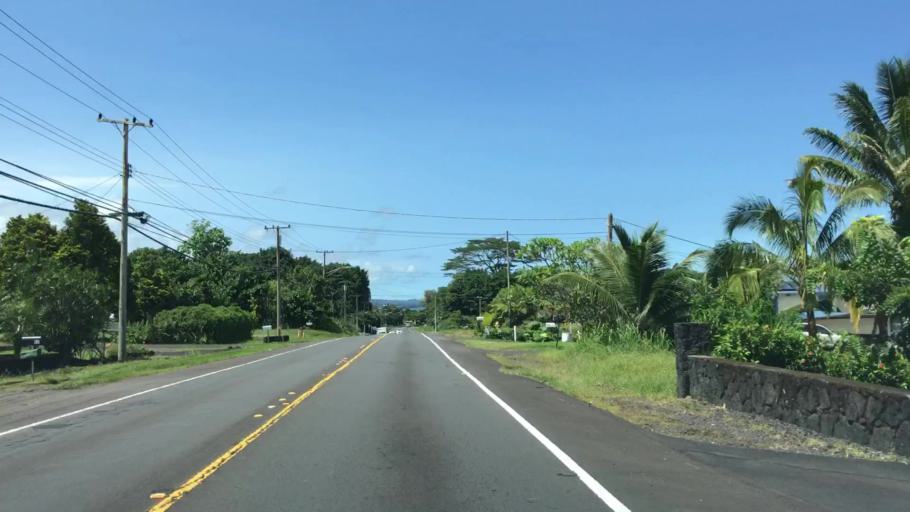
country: US
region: Hawaii
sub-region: Hawaii County
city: Hilo
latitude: 19.6915
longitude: -155.0811
